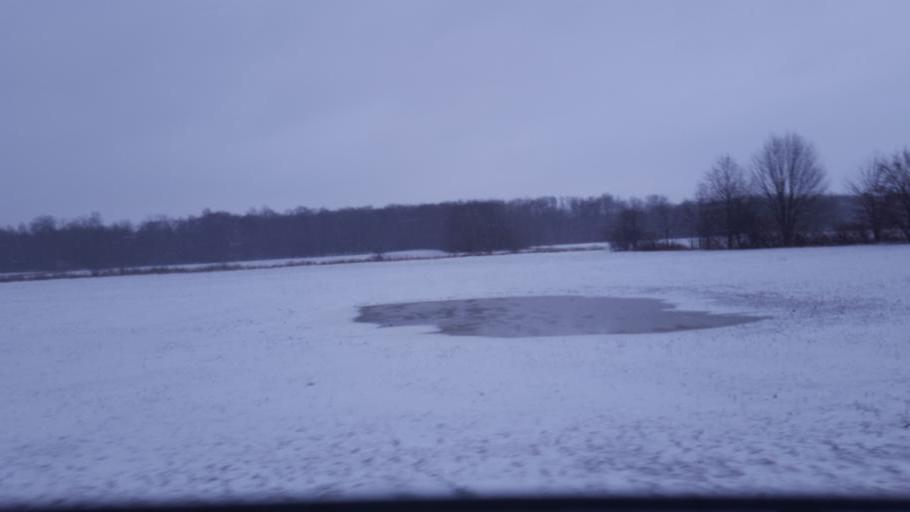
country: US
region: Ohio
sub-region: Morrow County
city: Mount Gilead
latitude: 40.5273
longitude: -82.7926
